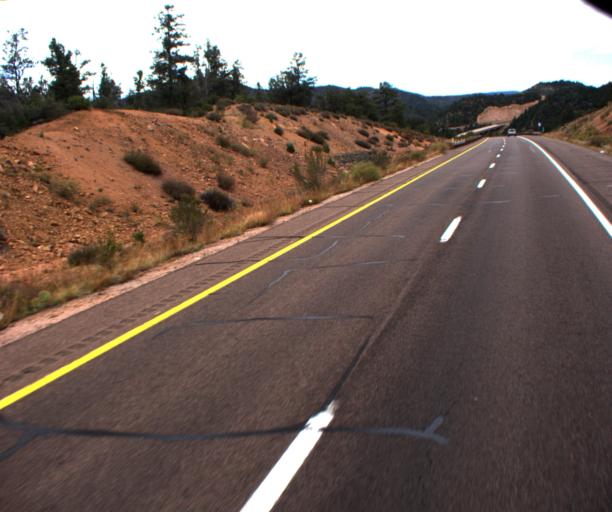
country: US
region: Arizona
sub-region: Gila County
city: Star Valley
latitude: 34.2729
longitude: -111.1769
